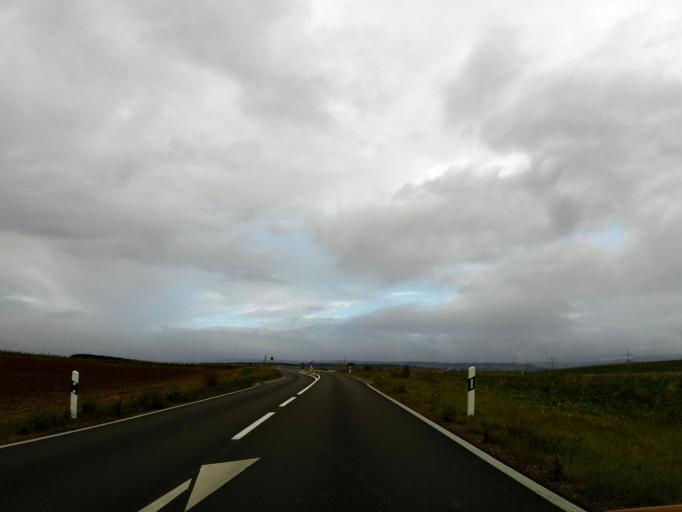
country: DE
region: Rheinland-Pfalz
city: Hargesheim
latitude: 49.8747
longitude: 7.8402
